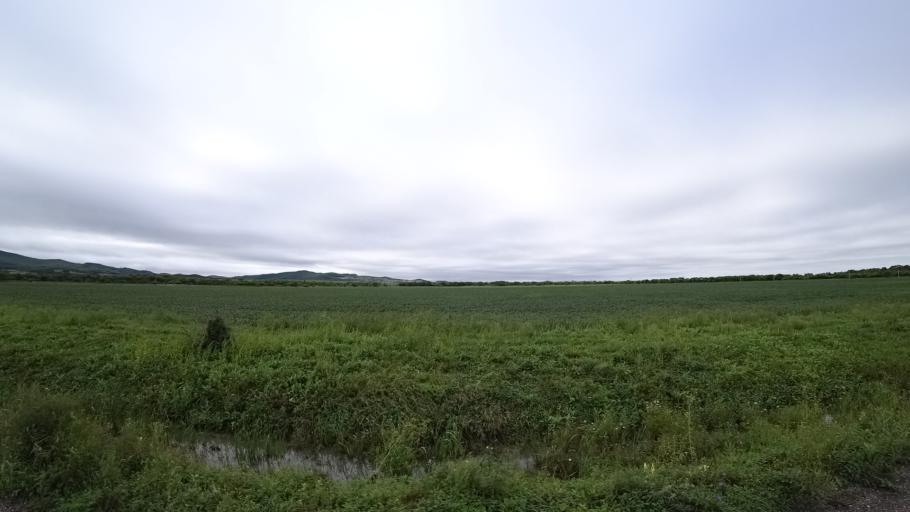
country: RU
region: Primorskiy
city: Monastyrishche
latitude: 44.1800
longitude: 132.4844
